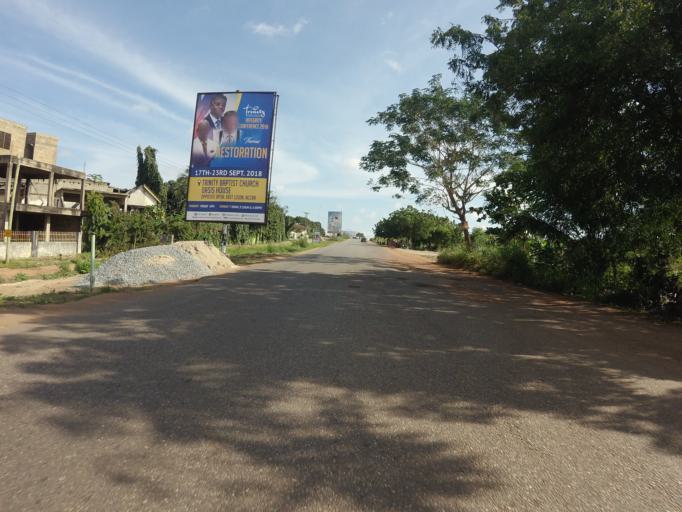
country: GH
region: Greater Accra
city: Medina Estates
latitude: 5.6508
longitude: -0.1692
